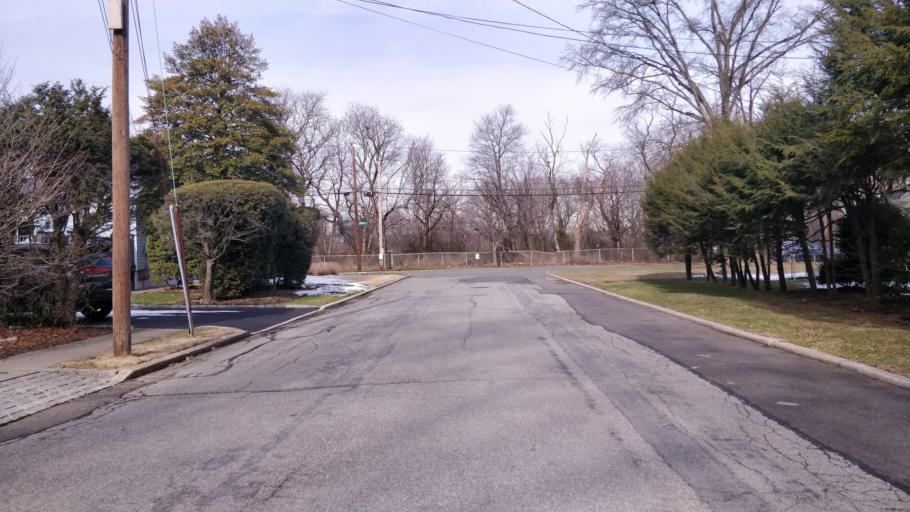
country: US
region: New York
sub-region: Nassau County
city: Jericho
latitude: 40.7835
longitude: -73.5290
